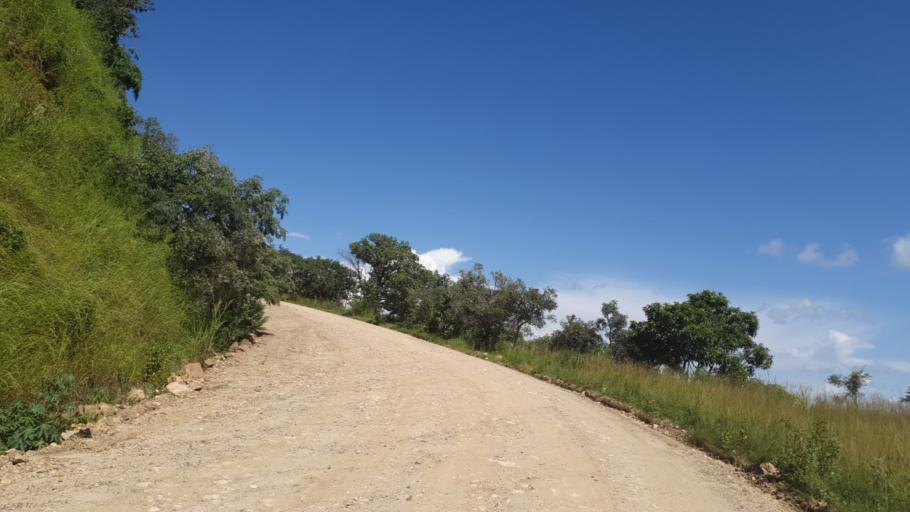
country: ET
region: Oromiya
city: Shambu
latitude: 9.7105
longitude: 36.6279
